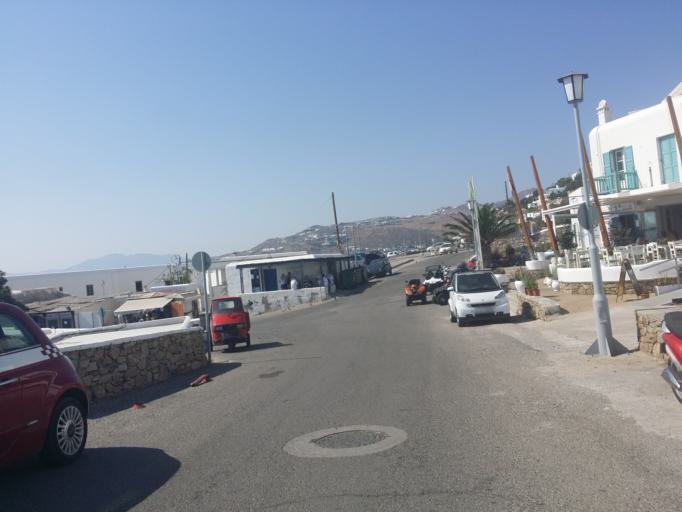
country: GR
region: South Aegean
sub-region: Nomos Kykladon
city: Mykonos
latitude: 37.4509
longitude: 25.3290
